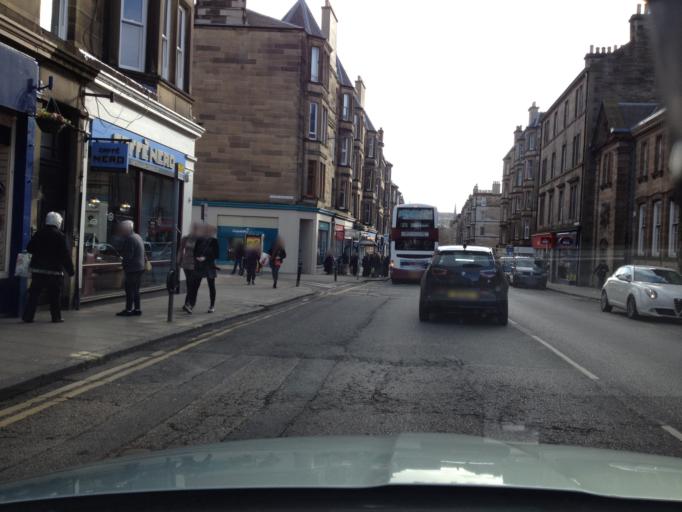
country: GB
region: Scotland
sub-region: Edinburgh
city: Edinburgh
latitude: 55.9293
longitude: -3.2096
